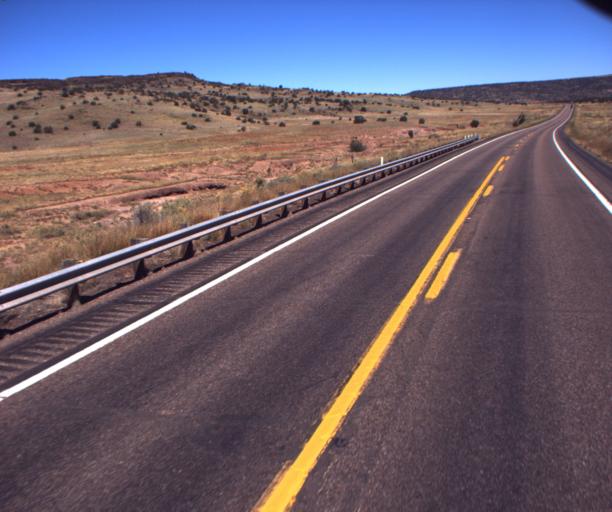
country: US
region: Arizona
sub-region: Apache County
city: Saint Johns
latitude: 34.3395
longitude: -109.3851
